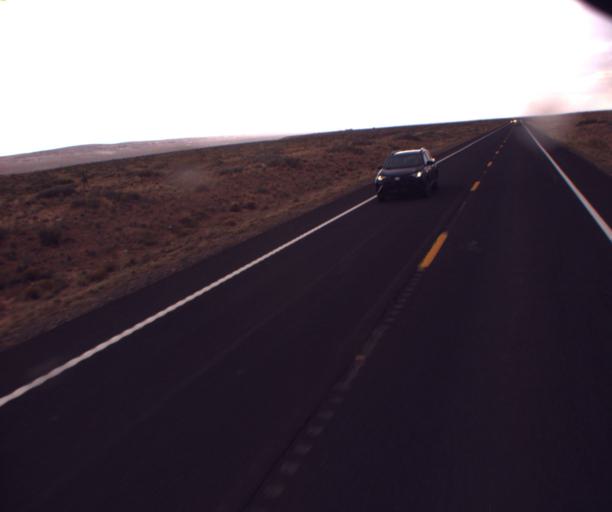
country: US
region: Arizona
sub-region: Coconino County
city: Tuba City
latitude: 36.1740
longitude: -111.0836
